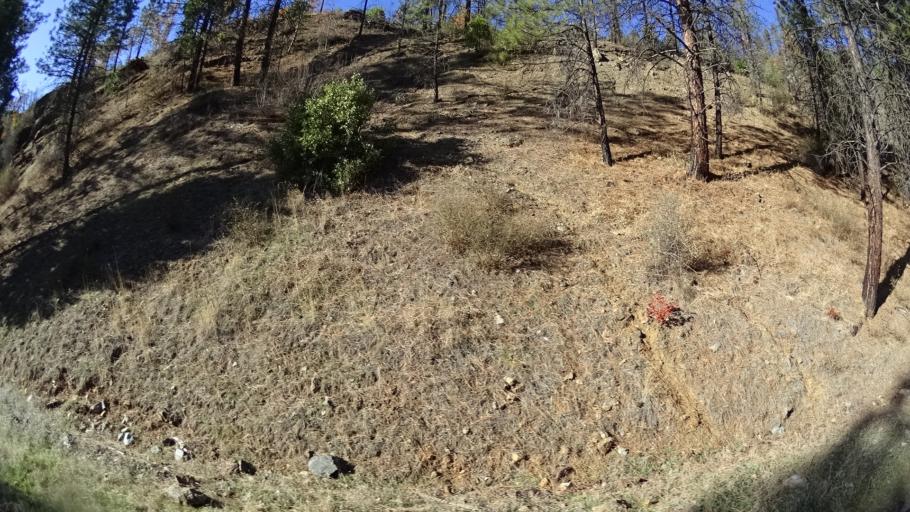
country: US
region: California
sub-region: Siskiyou County
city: Yreka
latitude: 41.8839
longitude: -122.8229
